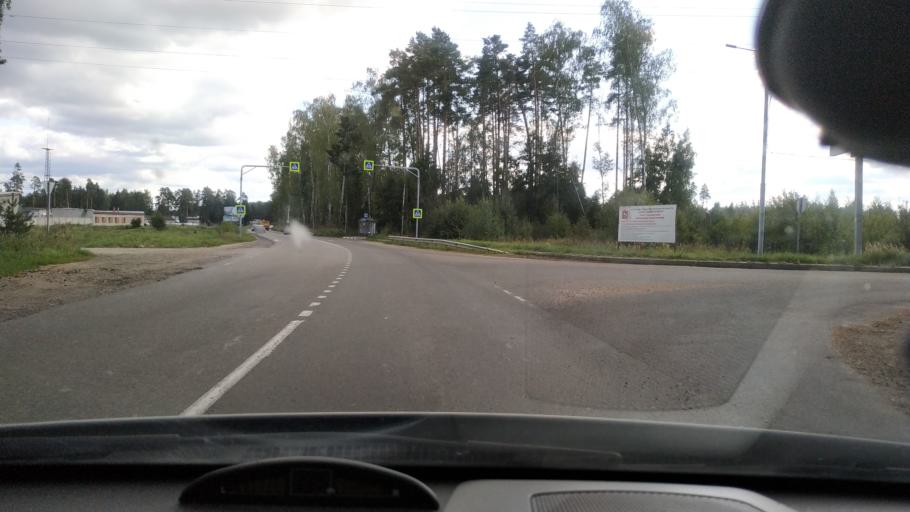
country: RU
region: Moskovskaya
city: Zheleznodorozhnyy
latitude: 55.7952
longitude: 38.0318
